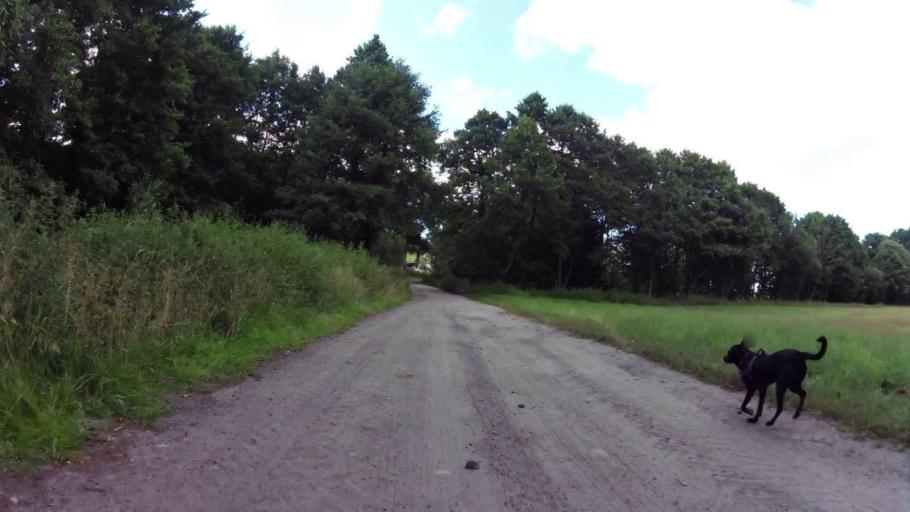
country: PL
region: West Pomeranian Voivodeship
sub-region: Powiat swidwinski
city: Swidwin
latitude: 53.6813
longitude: 15.7436
